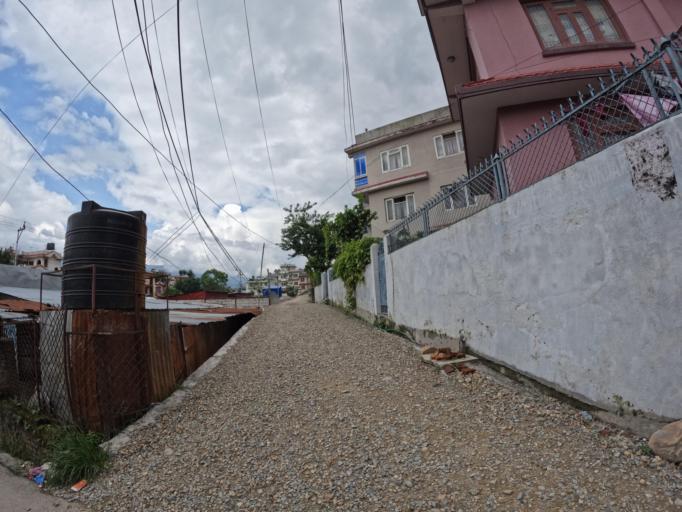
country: NP
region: Central Region
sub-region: Bagmati Zone
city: Kathmandu
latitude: 27.7444
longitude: 85.3167
